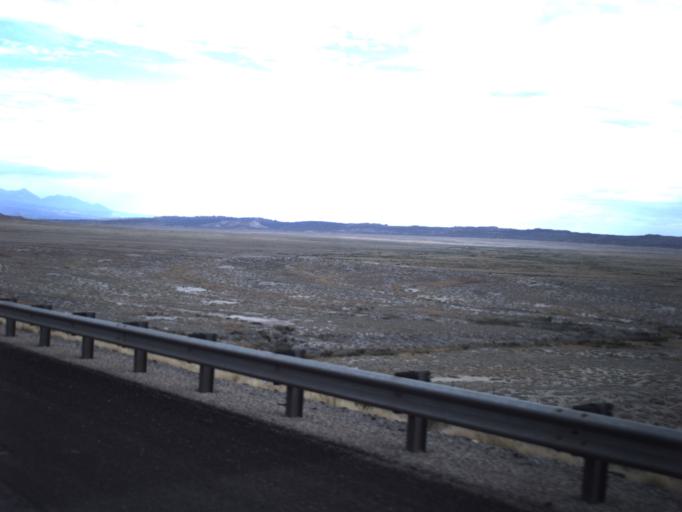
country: US
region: Utah
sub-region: Grand County
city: Moab
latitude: 38.9566
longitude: -109.7083
